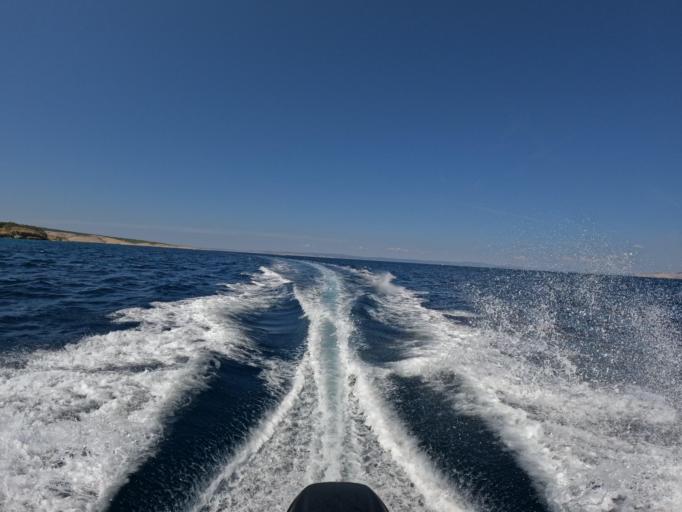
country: HR
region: Primorsko-Goranska
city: Lopar
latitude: 44.8551
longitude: 14.7269
